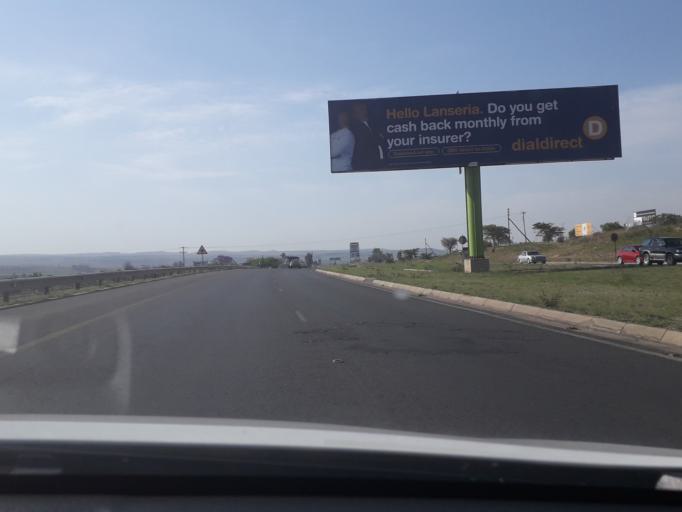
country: ZA
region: Gauteng
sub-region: City of Johannesburg Metropolitan Municipality
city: Diepsloot
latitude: -25.9550
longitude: 27.9138
